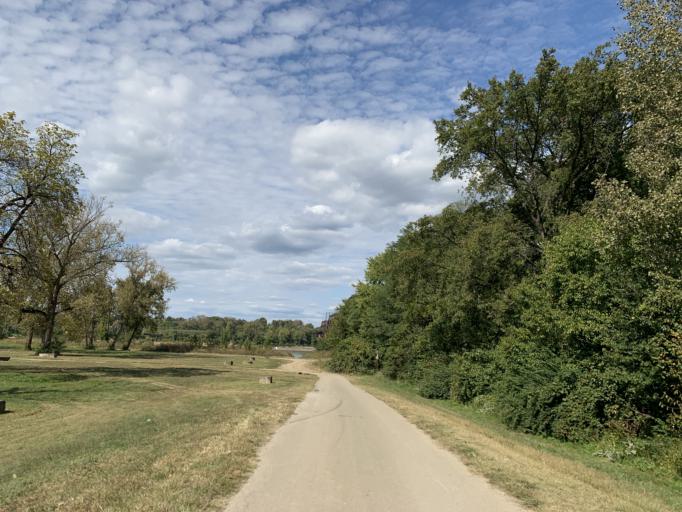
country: US
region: Indiana
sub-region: Floyd County
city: New Albany
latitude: 38.2780
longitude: -85.8013
